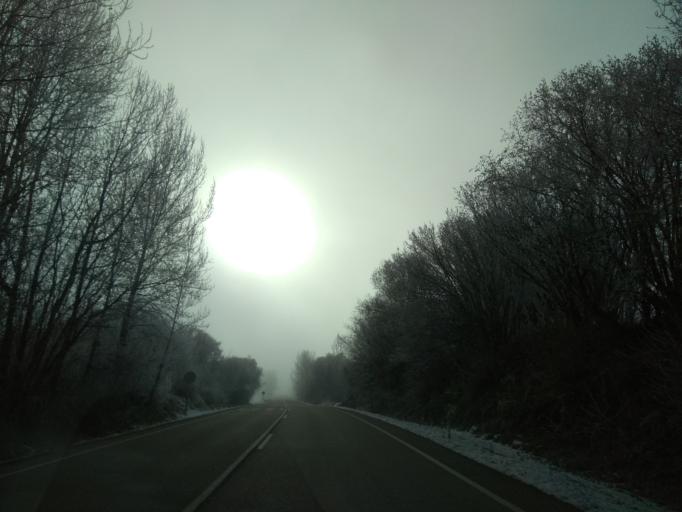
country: ES
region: Castille and Leon
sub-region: Provincia de Burgos
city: Medina de Pomar
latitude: 43.0039
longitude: -3.5198
